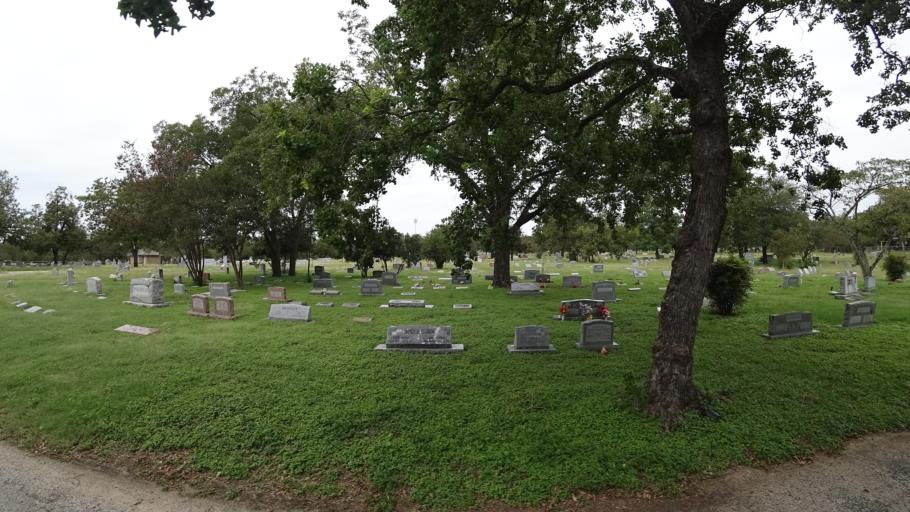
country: US
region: Texas
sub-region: Travis County
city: Austin
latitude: 30.2767
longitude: -97.7232
